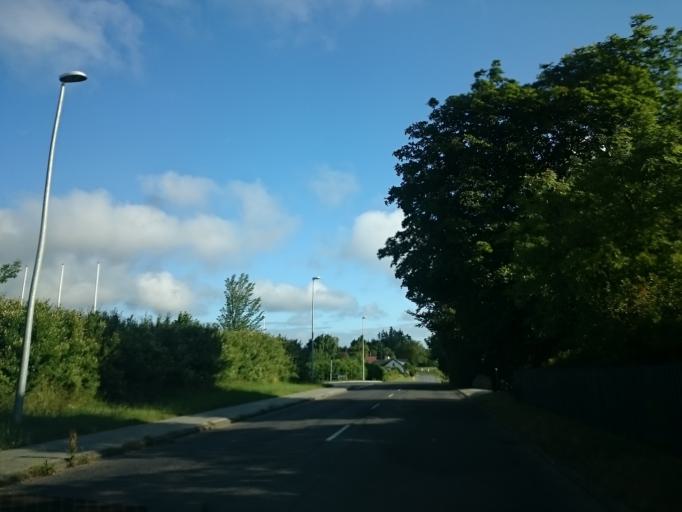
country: DK
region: Central Jutland
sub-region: Arhus Kommune
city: Tranbjerg
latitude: 56.1095
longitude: 10.1107
